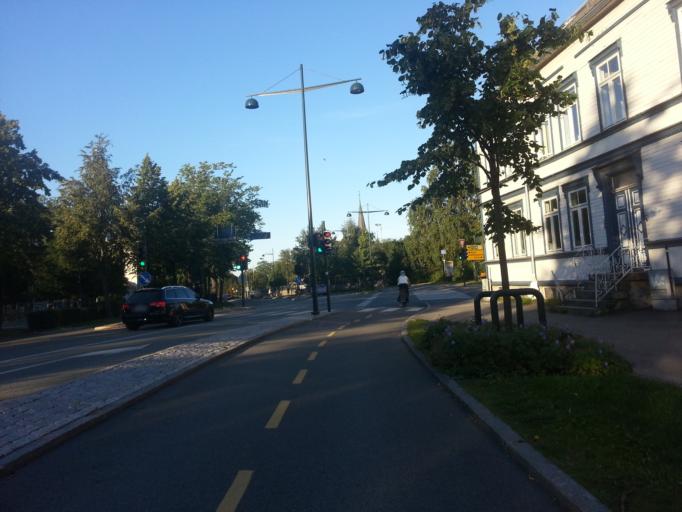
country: NO
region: Sor-Trondelag
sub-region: Trondheim
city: Trondheim
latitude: 63.4289
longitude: 10.3704
